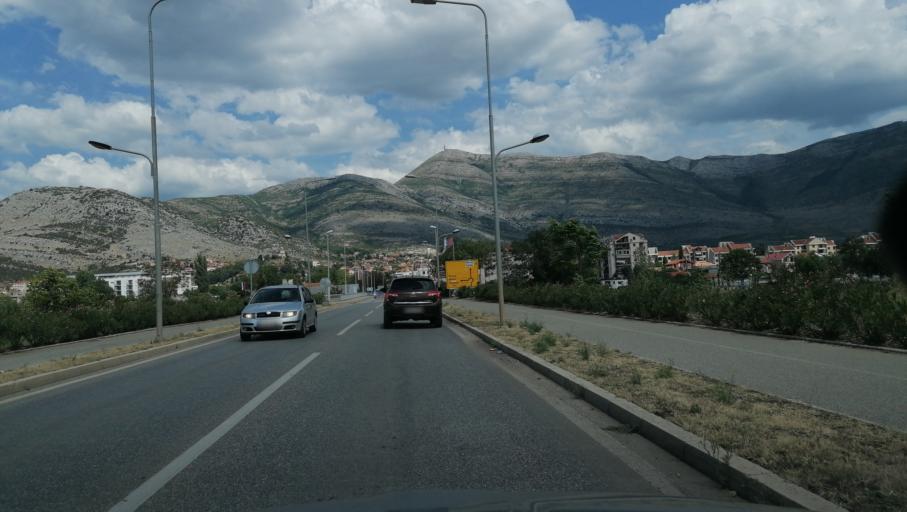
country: BA
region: Republika Srpska
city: Trebinje
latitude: 42.7030
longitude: 18.3432
